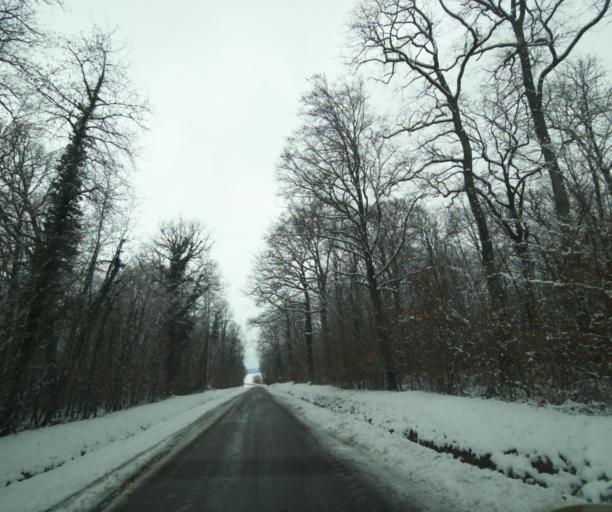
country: FR
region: Champagne-Ardenne
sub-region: Departement de la Haute-Marne
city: Laneuville-a-Remy
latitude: 48.3933
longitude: 4.8677
